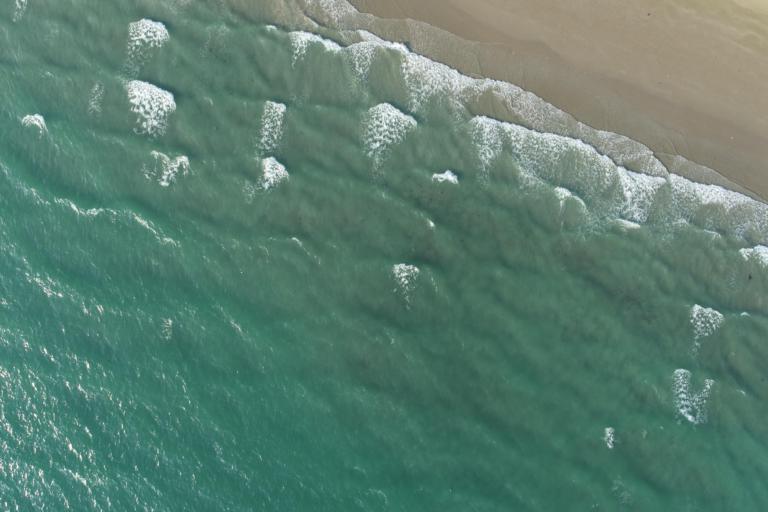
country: TH
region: Rayong
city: Rayong
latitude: 12.6023
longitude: 101.3990
